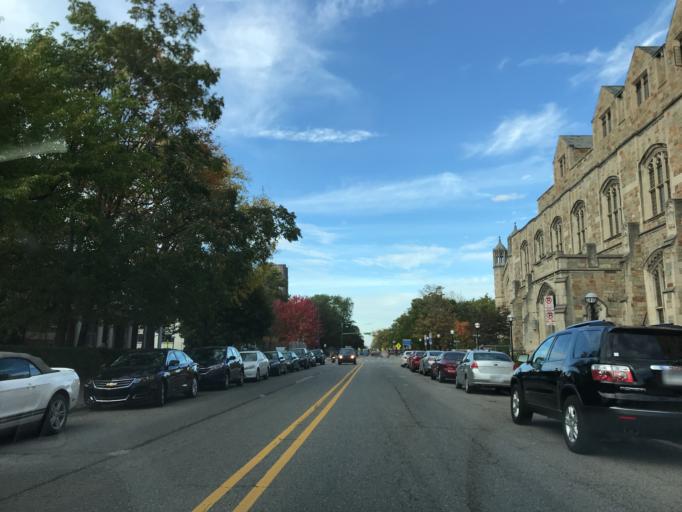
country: US
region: Michigan
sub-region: Washtenaw County
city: Ann Arbor
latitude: 42.2734
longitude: -83.7406
